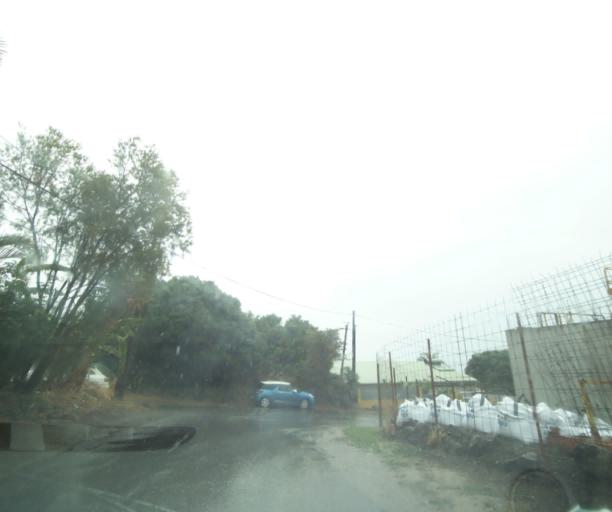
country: RE
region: Reunion
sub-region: Reunion
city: Saint-Paul
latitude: -20.9897
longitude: 55.3244
